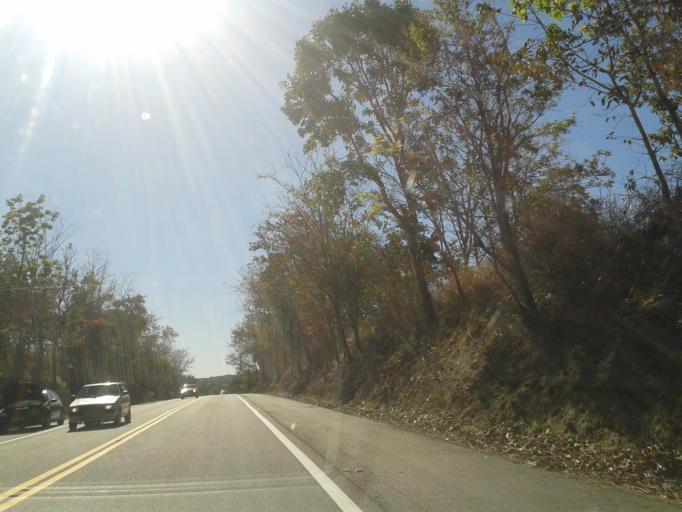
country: BR
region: Goias
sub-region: Goias
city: Goias
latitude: -15.7631
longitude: -50.1573
